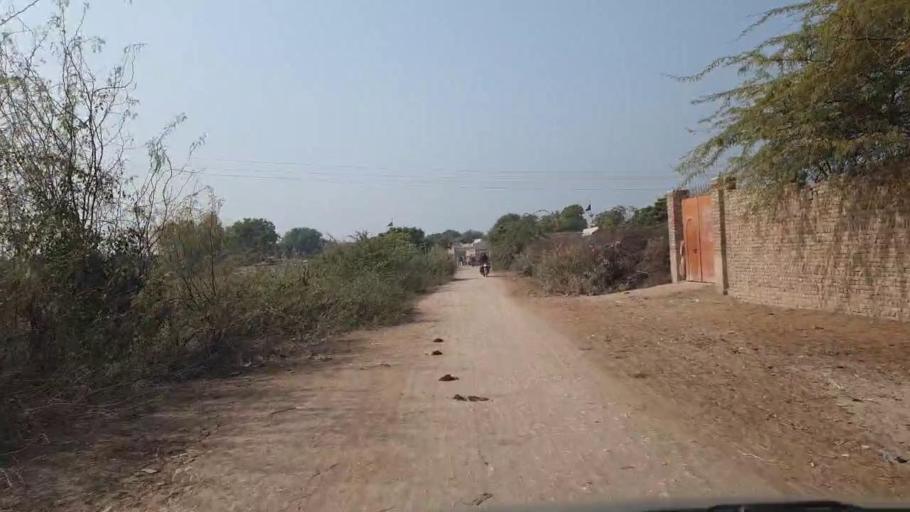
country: PK
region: Sindh
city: Bhit Shah
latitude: 25.8302
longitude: 68.4905
